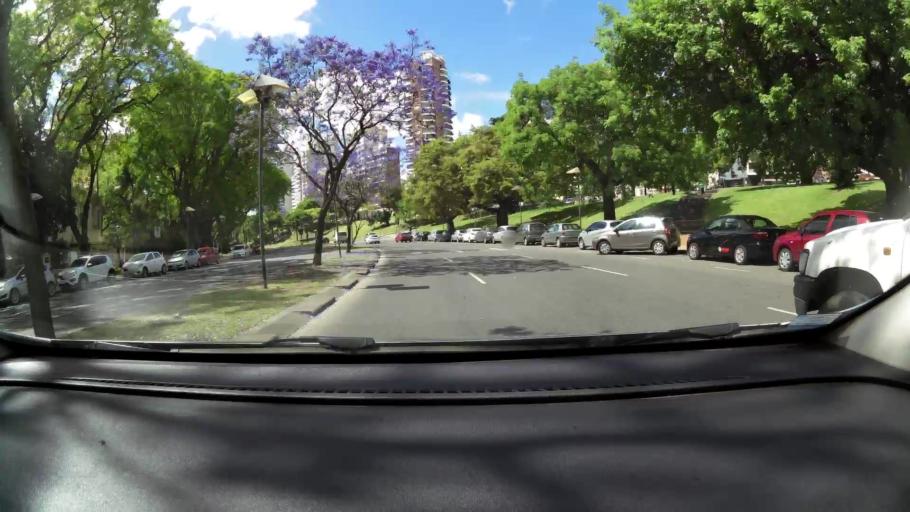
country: AR
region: Santa Fe
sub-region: Departamento de Rosario
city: Rosario
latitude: -32.9517
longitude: -60.6276
